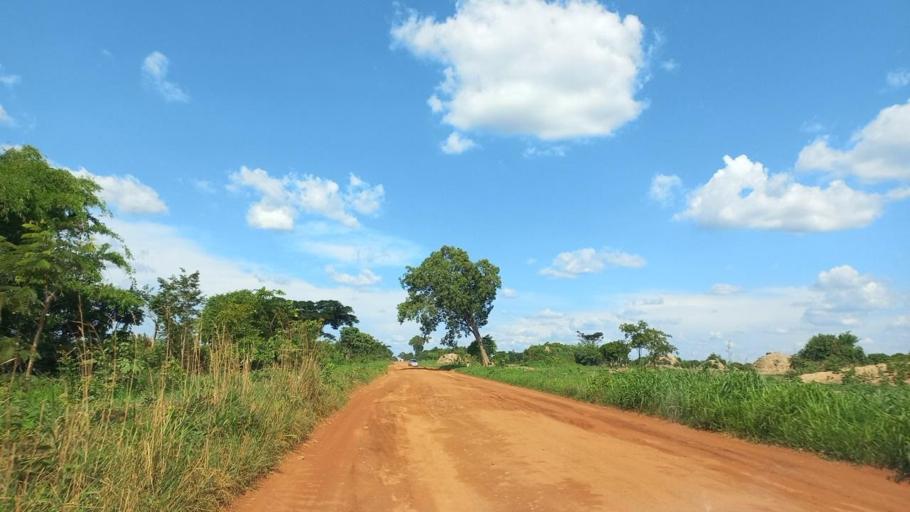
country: ZM
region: Copperbelt
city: Kitwe
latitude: -12.8695
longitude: 28.3616
